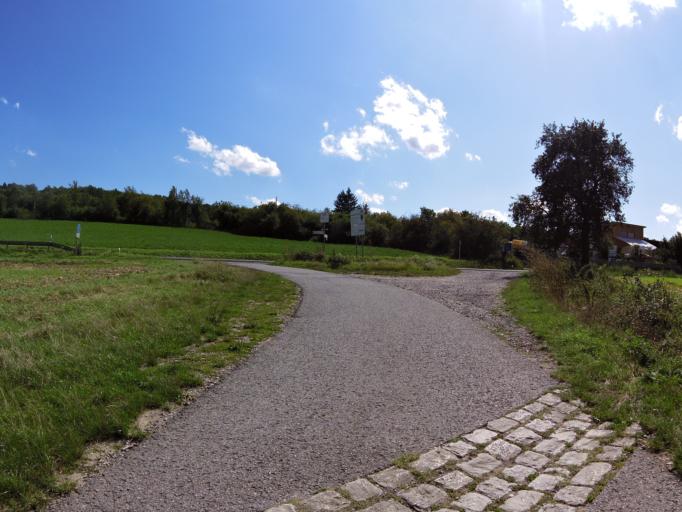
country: DE
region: Bavaria
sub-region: Regierungsbezirk Unterfranken
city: Frickenhausen
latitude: 49.6676
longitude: 10.0922
